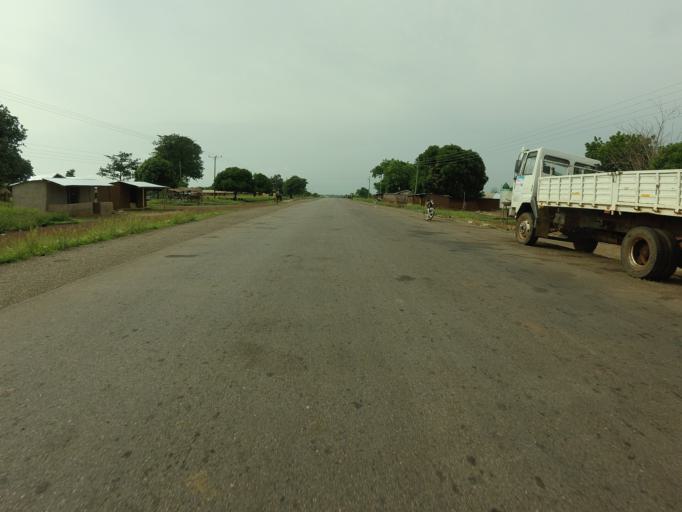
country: GH
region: Northern
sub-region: Yendi
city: Yendi
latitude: 9.6393
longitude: -0.0643
